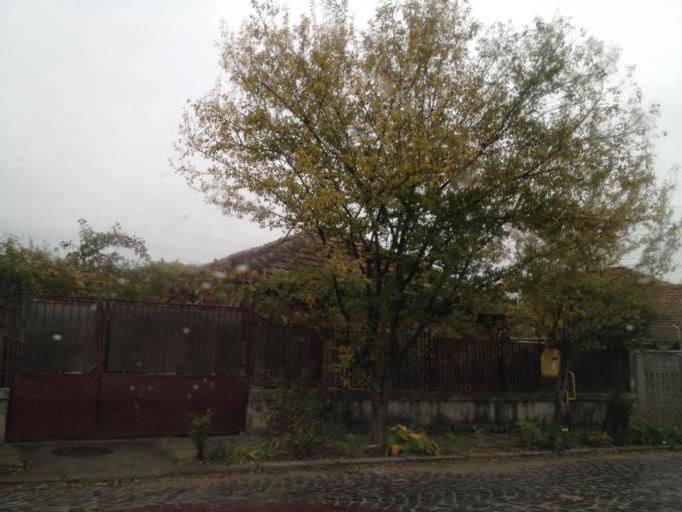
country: RO
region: Dolj
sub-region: Municipiul Craiova
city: Mofleni
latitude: 44.3097
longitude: 23.7768
